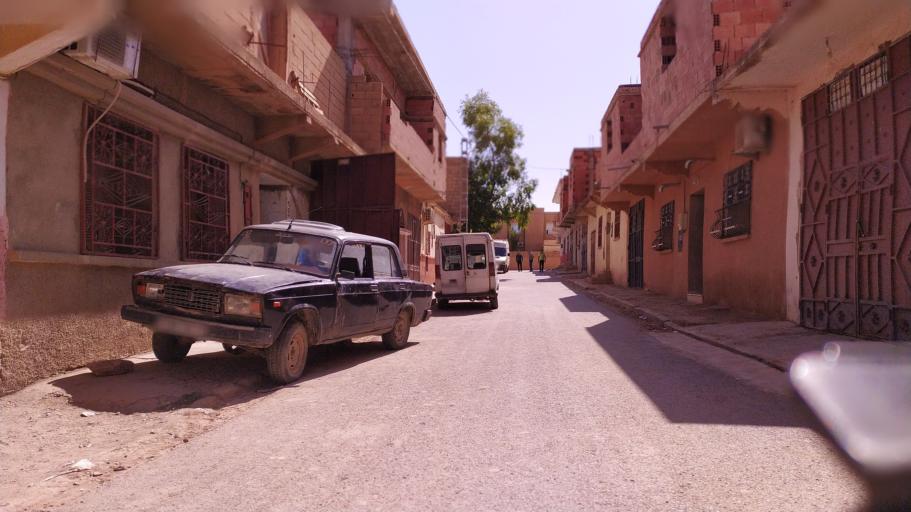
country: DZ
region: Tiaret
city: Frenda
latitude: 34.8964
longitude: 1.2390
